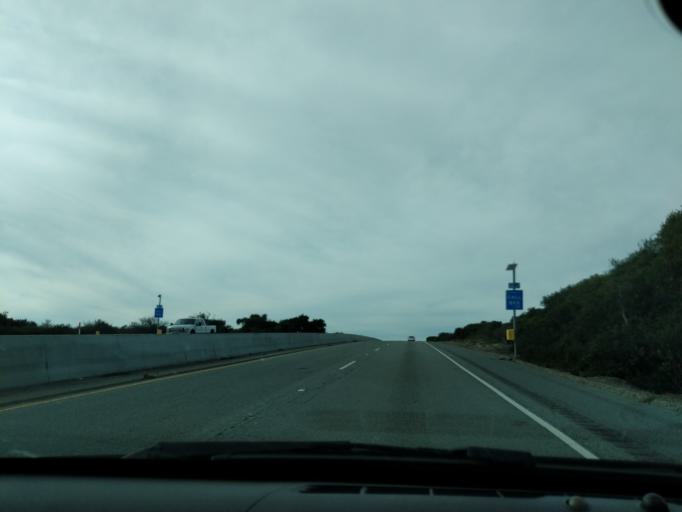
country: US
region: California
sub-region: Santa Barbara County
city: Vandenberg Village
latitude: 34.7059
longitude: -120.4820
